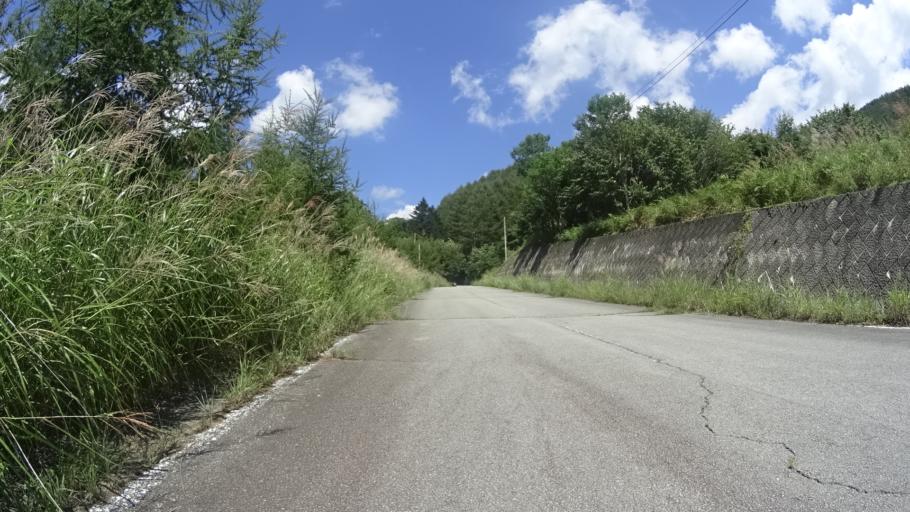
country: JP
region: Yamanashi
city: Enzan
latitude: 35.8137
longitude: 138.6546
